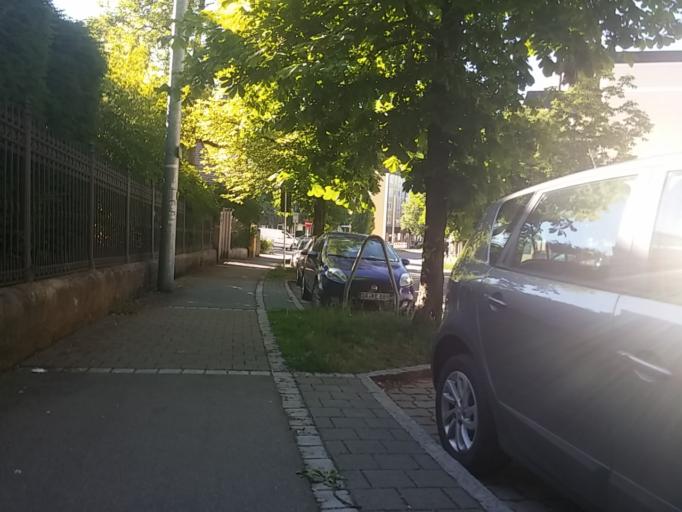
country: DE
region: Bavaria
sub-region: Swabia
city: Kempten (Allgaeu)
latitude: 47.7221
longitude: 10.3116
